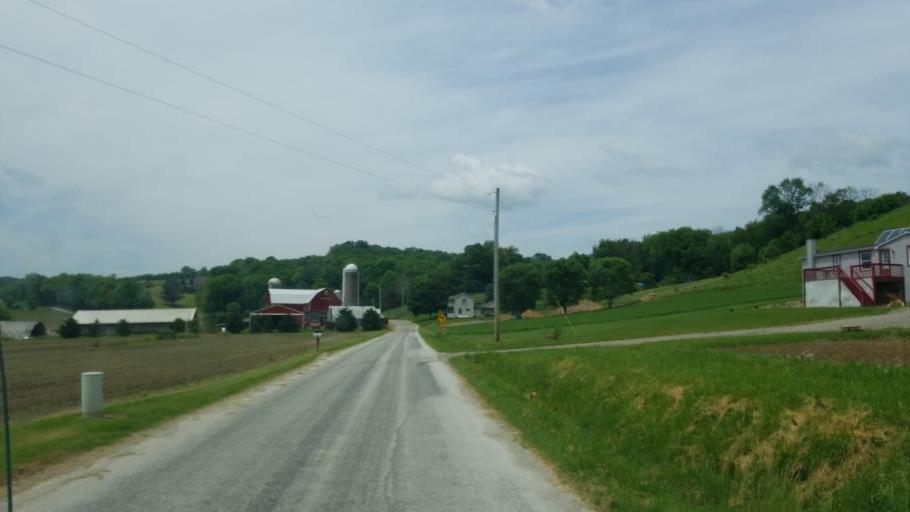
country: US
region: Ohio
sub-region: Coshocton County
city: West Lafayette
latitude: 40.3787
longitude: -81.7638
